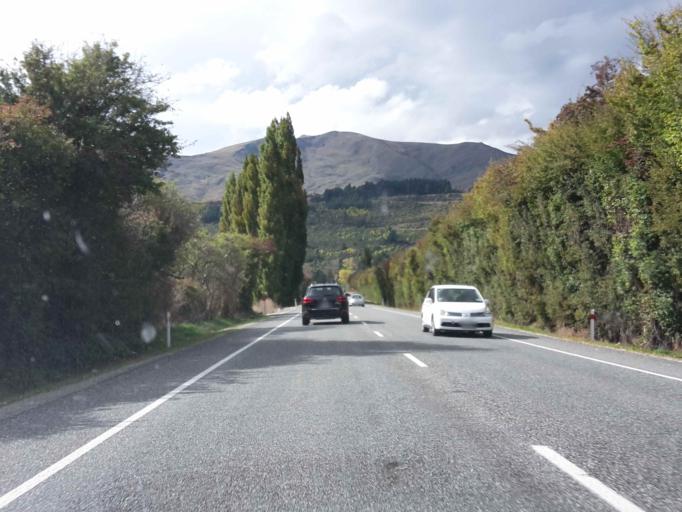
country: NZ
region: Otago
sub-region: Queenstown-Lakes District
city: Arrowtown
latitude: -44.9808
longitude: 168.8412
